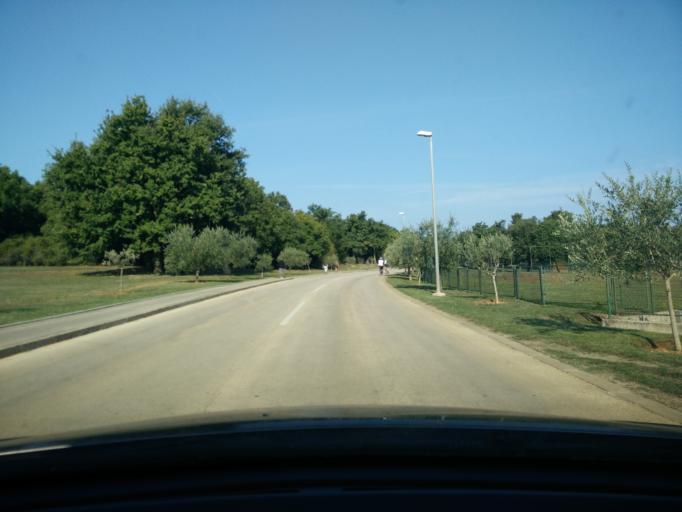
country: HR
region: Istarska
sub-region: Grad Porec
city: Porec
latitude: 45.1943
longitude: 13.5958
